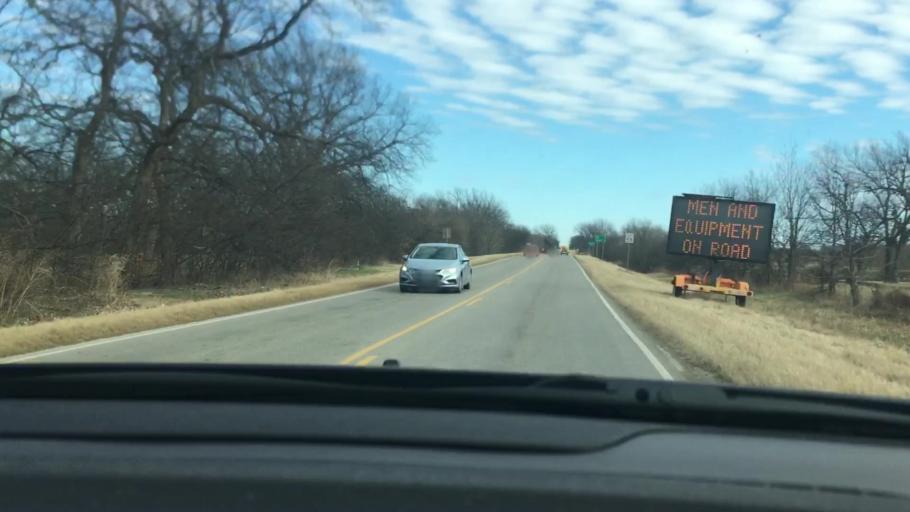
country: US
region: Oklahoma
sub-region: Garvin County
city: Stratford
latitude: 34.7966
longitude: -96.9472
